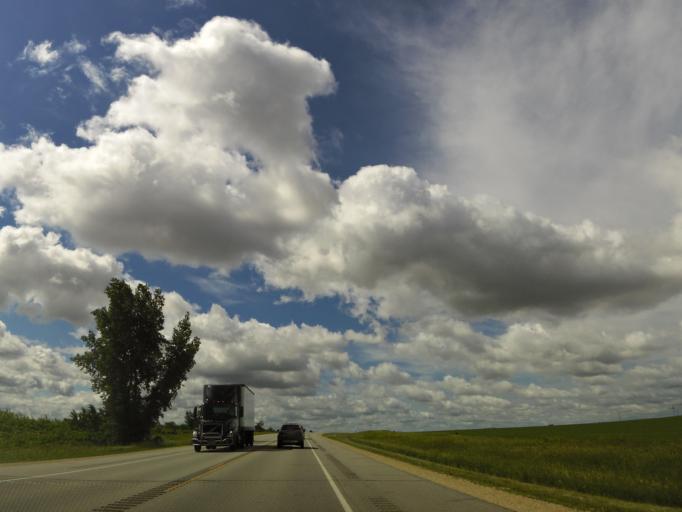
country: US
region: Minnesota
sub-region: Olmsted County
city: Stewartville
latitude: 43.8025
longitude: -92.4898
